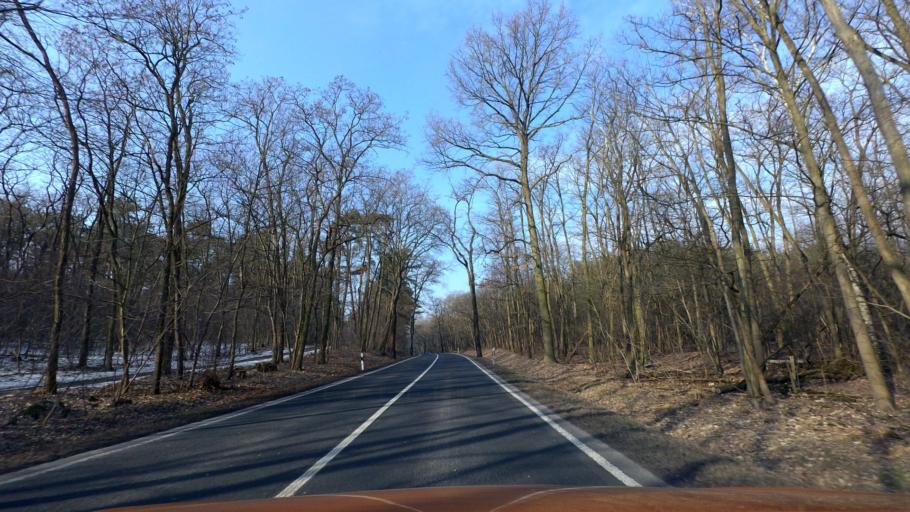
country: DE
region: Brandenburg
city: Ludwigsfelde
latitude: 52.2763
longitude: 13.2978
